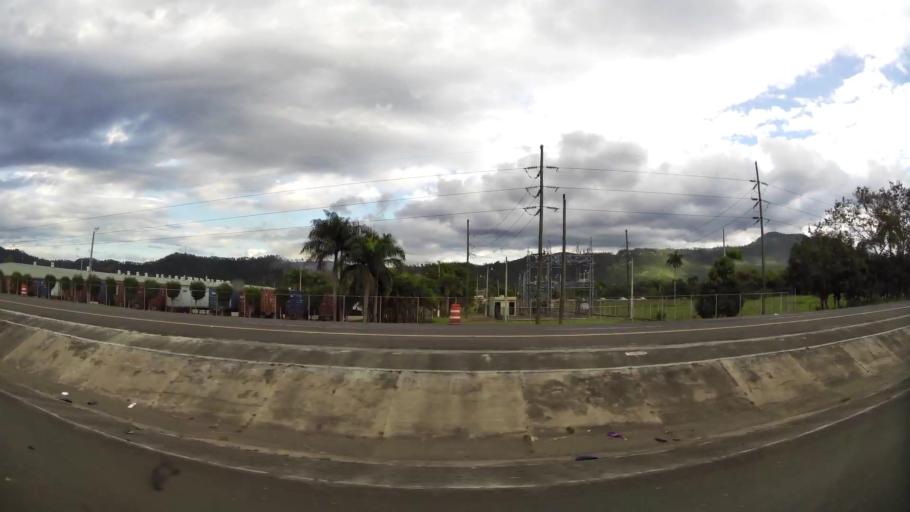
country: DO
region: Monsenor Nouel
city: Bonao
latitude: 18.9103
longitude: -70.3764
